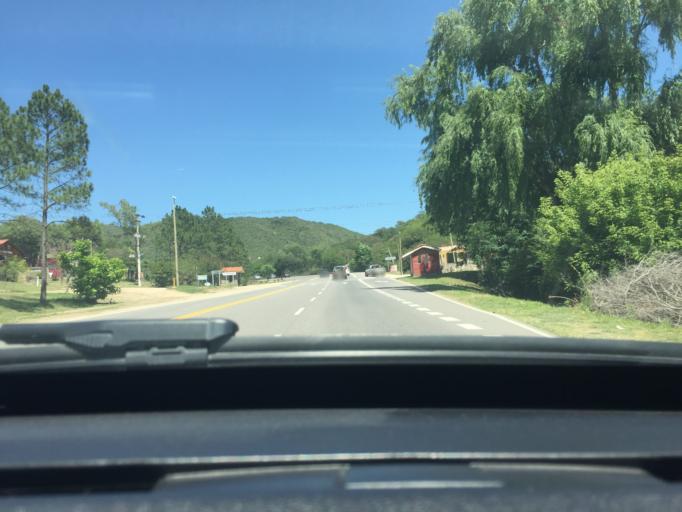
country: AR
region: Cordoba
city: Alta Gracia
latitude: -31.7412
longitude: -64.4571
